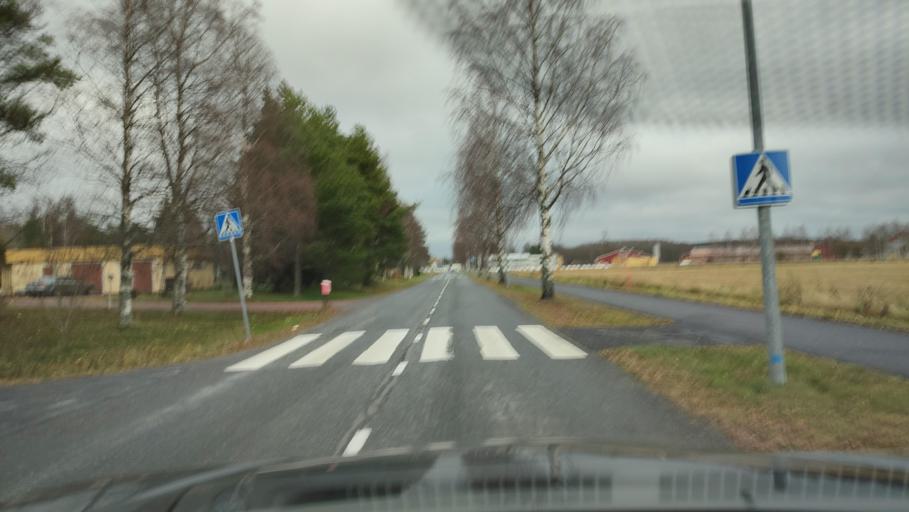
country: FI
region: Southern Ostrobothnia
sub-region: Suupohja
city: Kauhajoki
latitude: 62.4150
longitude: 22.1804
